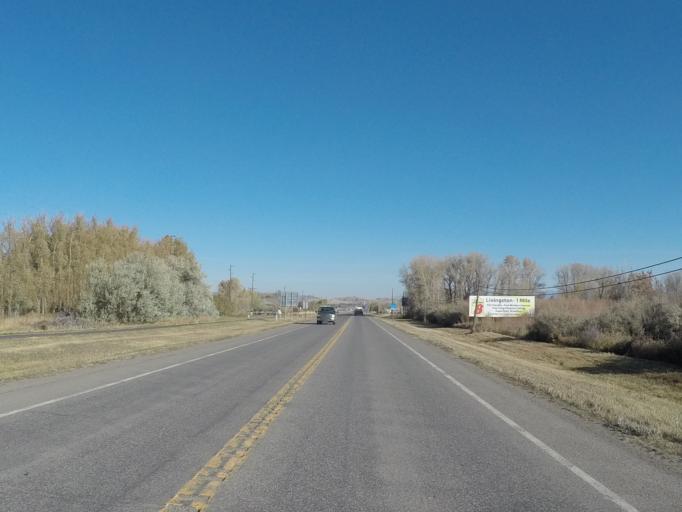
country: US
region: Montana
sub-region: Park County
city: Livingston
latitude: 45.6282
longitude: -110.5771
